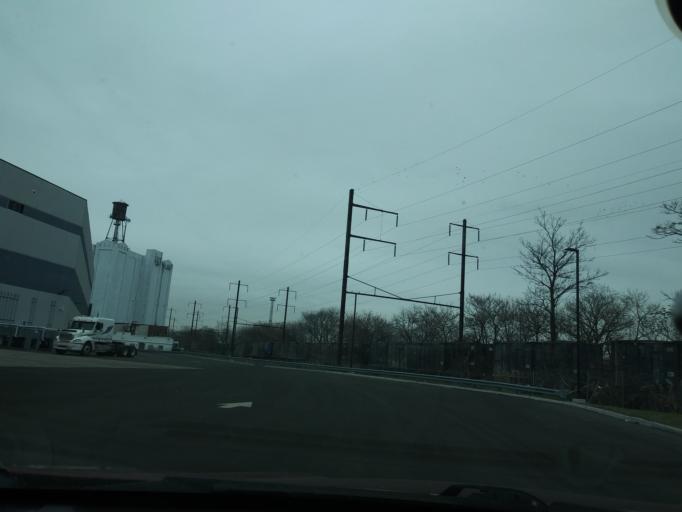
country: US
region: New Jersey
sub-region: Essex County
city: Newark
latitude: 40.7155
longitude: -74.1767
